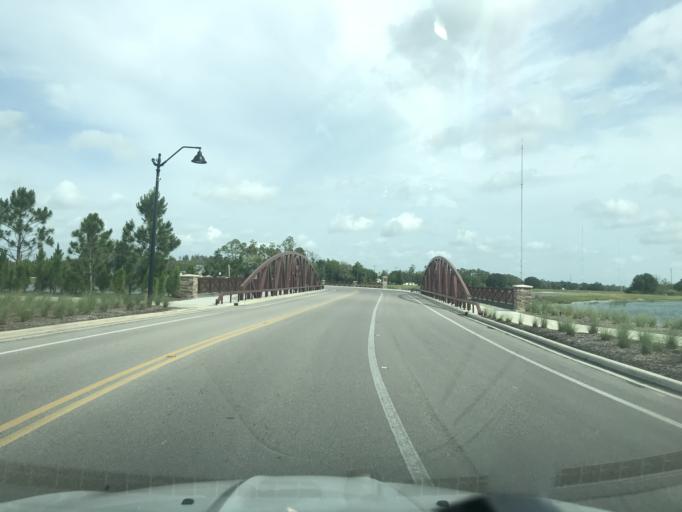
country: US
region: Florida
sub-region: Lee County
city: Fort Myers Shores
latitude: 26.7850
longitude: -81.7584
